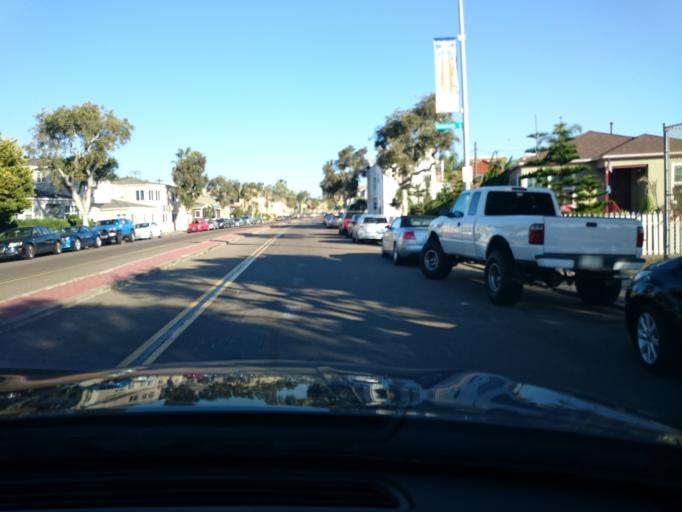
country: US
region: California
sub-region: San Diego County
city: La Jolla
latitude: 32.7751
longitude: -117.2520
